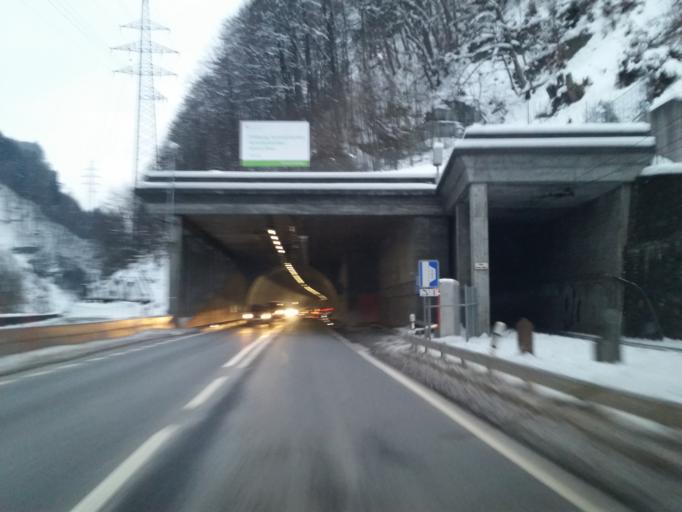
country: CH
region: Grisons
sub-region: Praettigau/Davos District
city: Grusch
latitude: 46.9760
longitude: 9.6207
